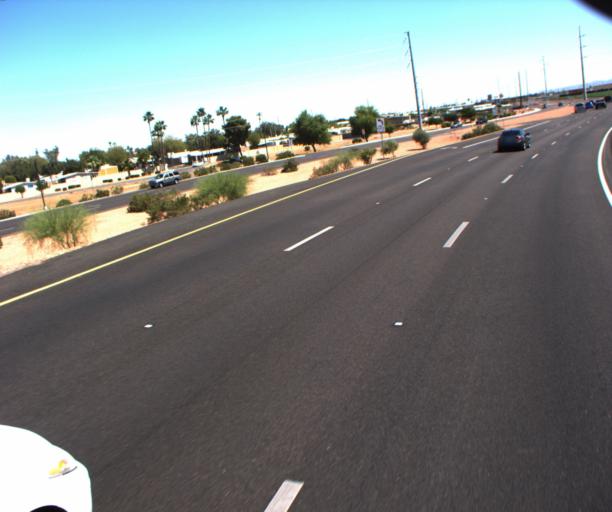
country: US
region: Arizona
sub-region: Maricopa County
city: Peoria
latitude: 33.5623
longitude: -112.2134
